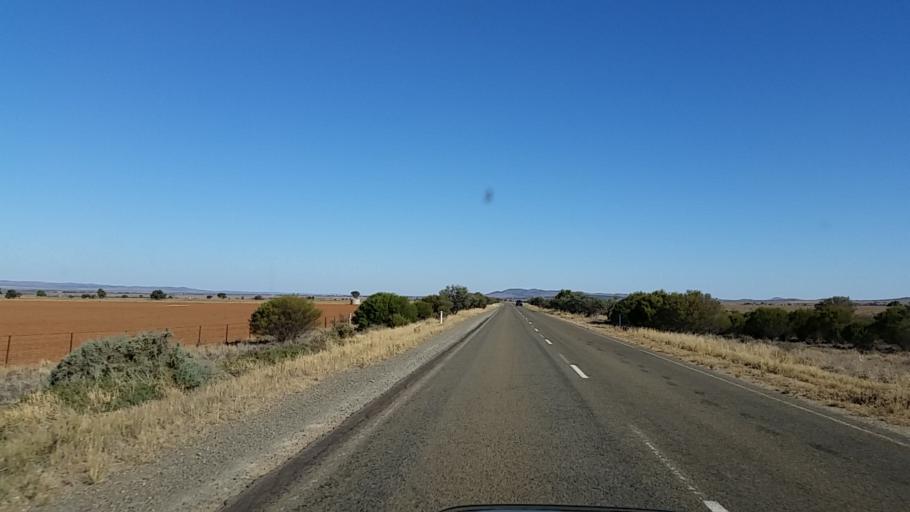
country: AU
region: South Australia
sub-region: Peterborough
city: Peterborough
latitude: -32.6442
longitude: 138.5998
